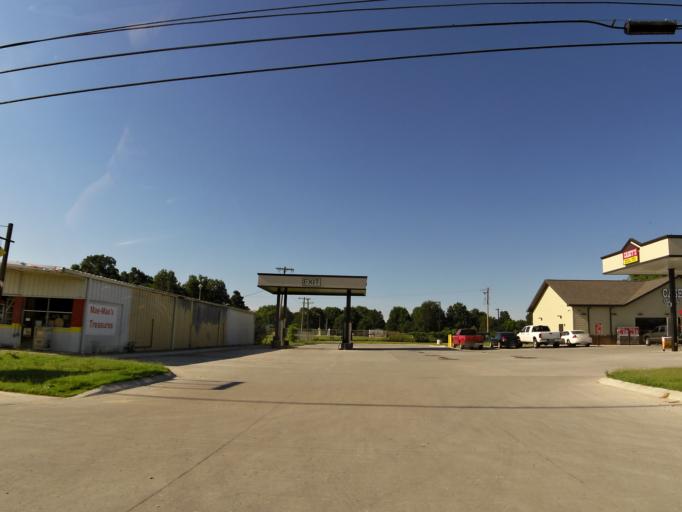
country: US
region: Arkansas
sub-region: Clay County
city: Corning
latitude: 36.4113
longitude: -90.5917
